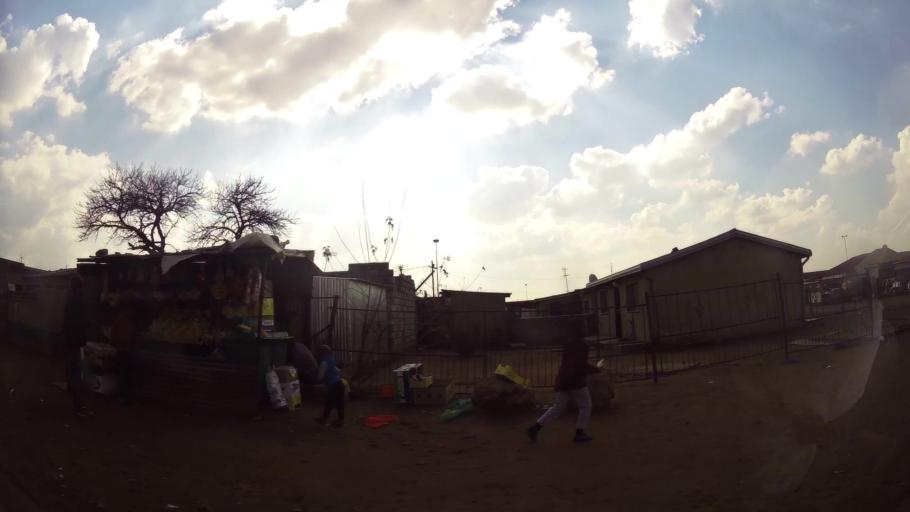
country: ZA
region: Gauteng
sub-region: Ekurhuleni Metropolitan Municipality
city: Germiston
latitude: -26.3519
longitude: 28.1489
